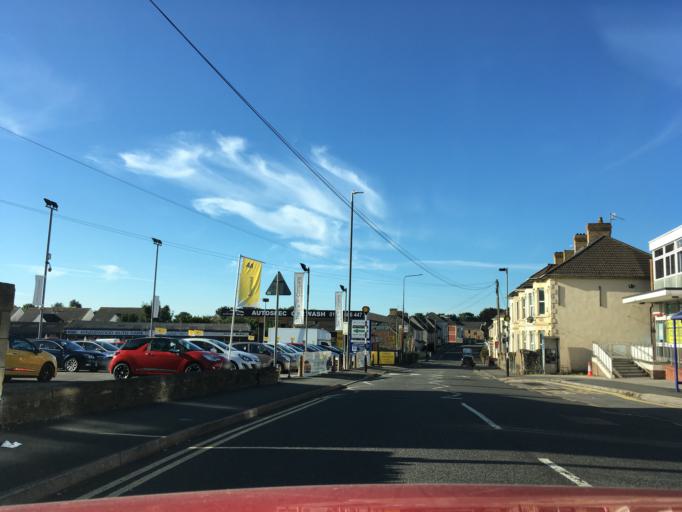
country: GB
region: England
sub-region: South Gloucestershire
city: Kingswood
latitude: 51.4615
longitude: -2.5055
